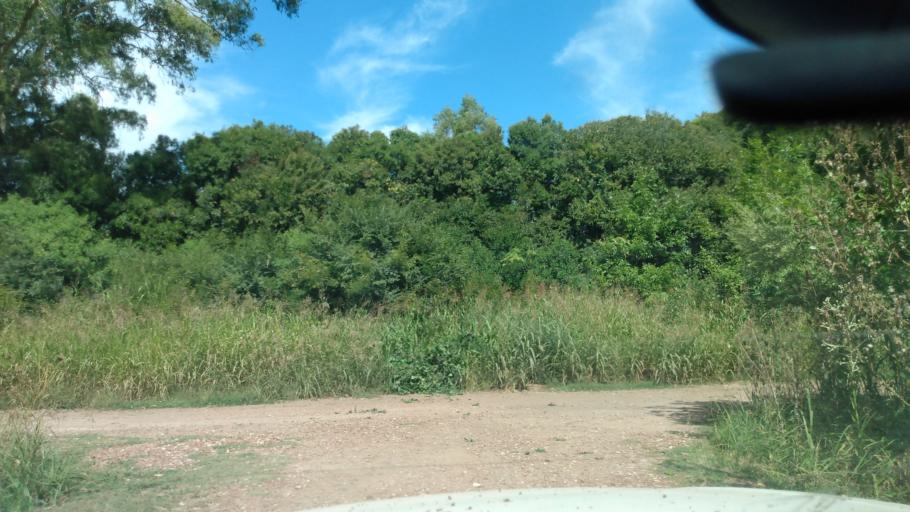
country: AR
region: Buenos Aires
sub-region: Partido de Lujan
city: Lujan
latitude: -34.5520
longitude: -59.1511
